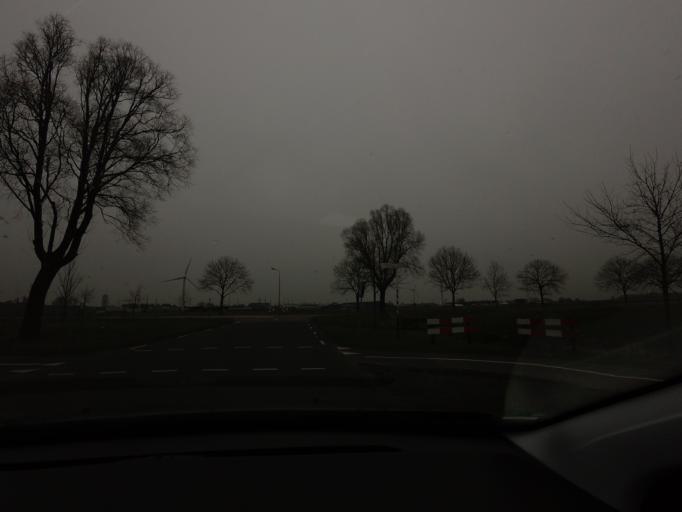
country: NL
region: Friesland
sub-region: Gemeente Franekeradeel
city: Franeker
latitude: 53.1787
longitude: 5.5577
